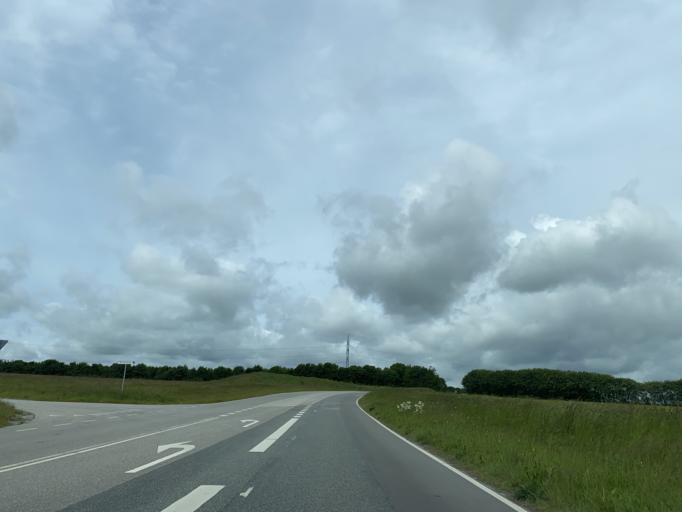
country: DK
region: Central Jutland
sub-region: Arhus Kommune
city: Trige
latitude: 56.1879
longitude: 10.1526
